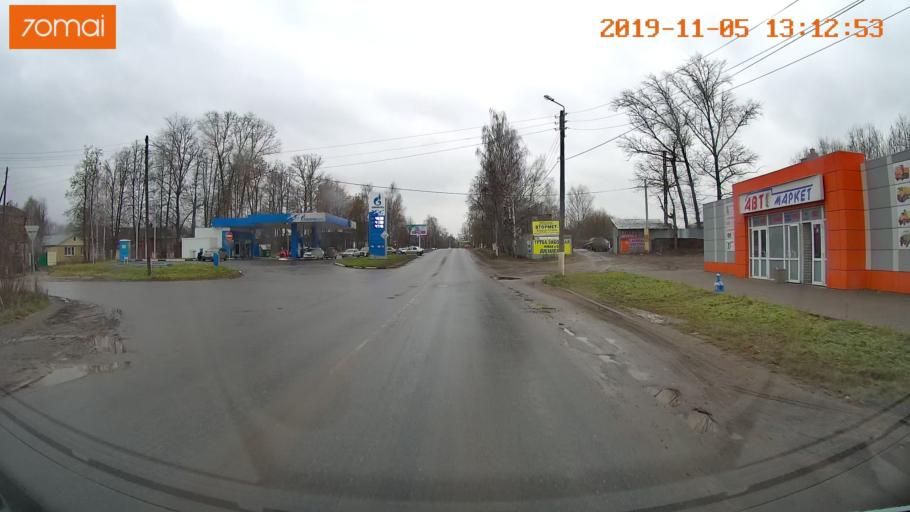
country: RU
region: Ivanovo
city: Shuya
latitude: 56.8548
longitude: 41.3532
